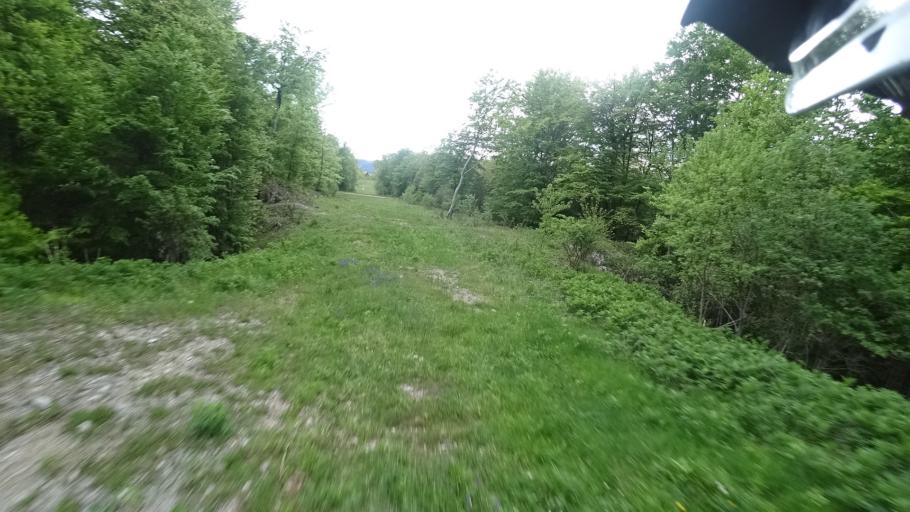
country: HR
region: Karlovacka
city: Plaski
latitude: 44.9063
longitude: 15.4168
